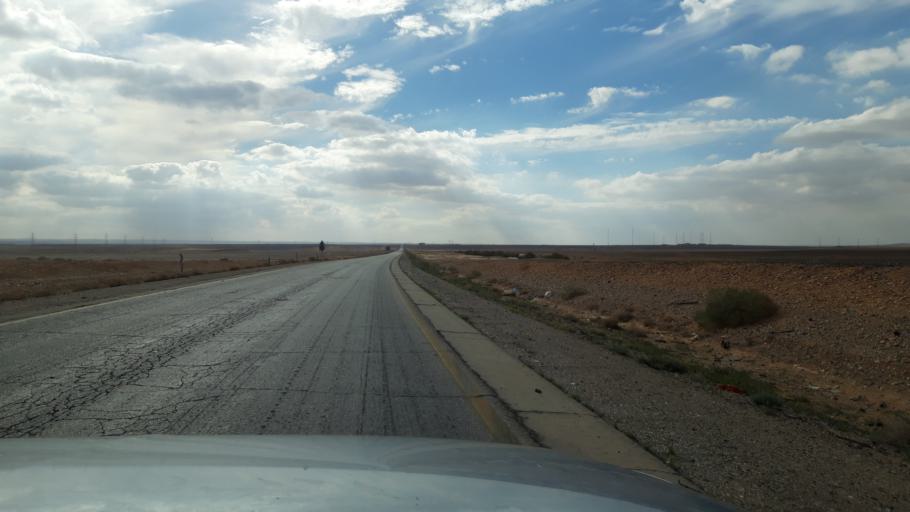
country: JO
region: Amman
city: Al Azraq ash Shamali
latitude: 31.7316
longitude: 36.5061
